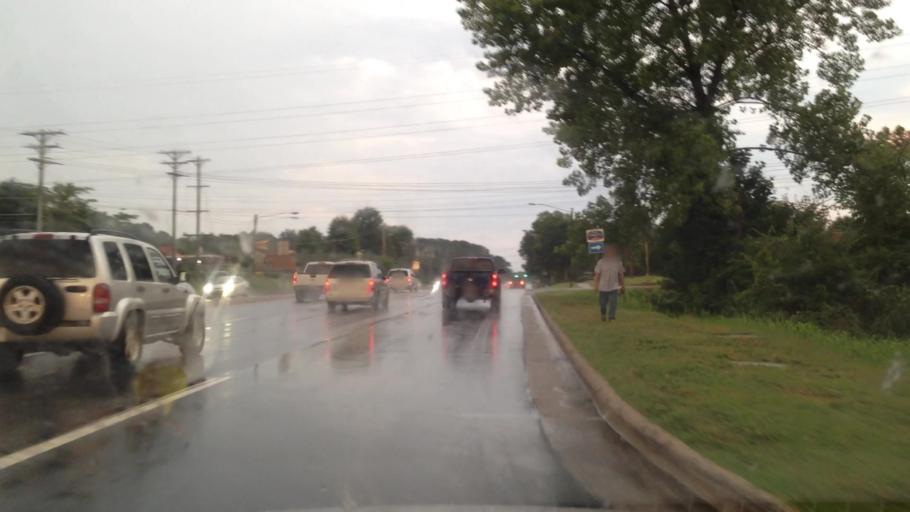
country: US
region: North Carolina
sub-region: Mecklenburg County
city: Pineville
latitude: 35.1373
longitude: -80.9067
